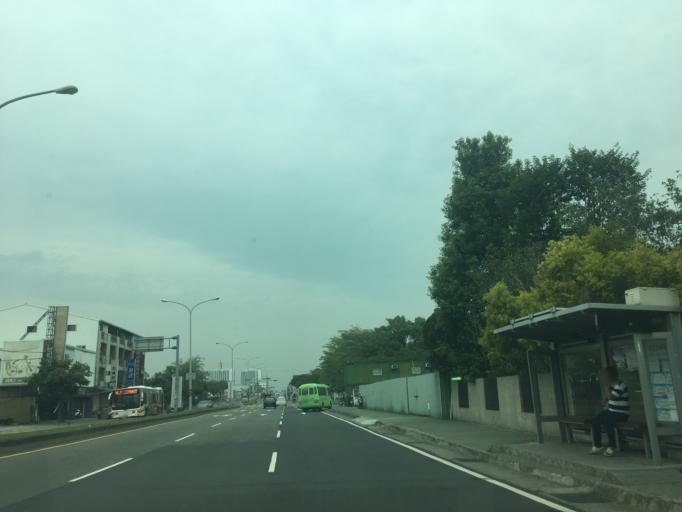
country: TW
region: Taiwan
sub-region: Taichung City
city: Taichung
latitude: 24.0759
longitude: 120.6999
